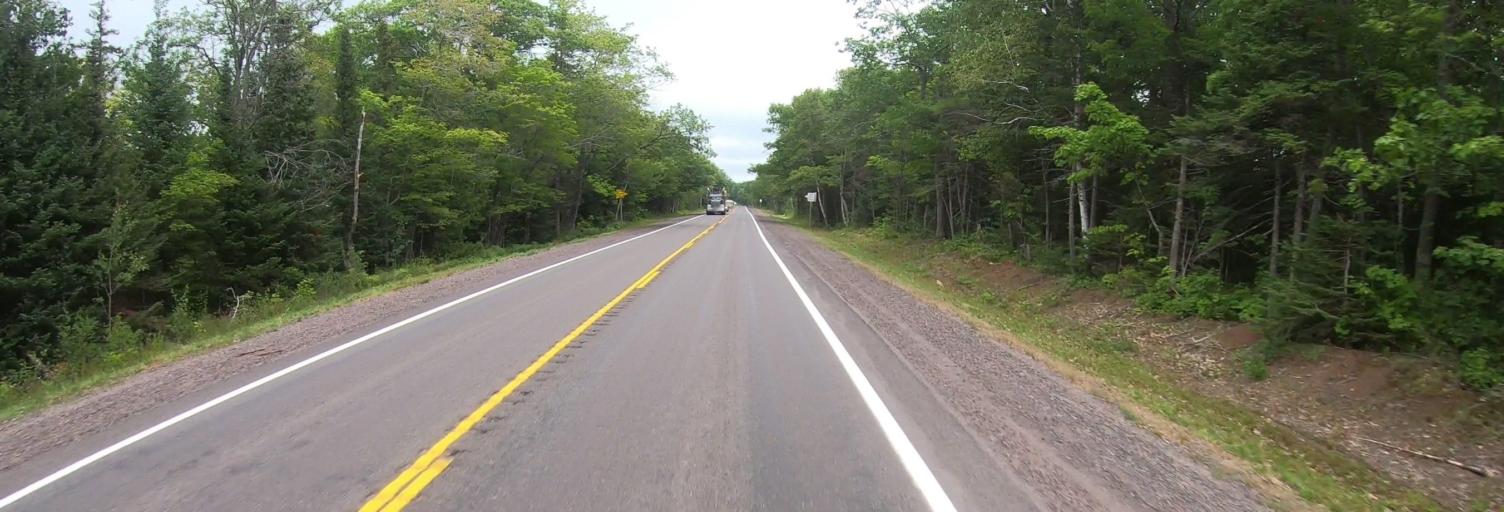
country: US
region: Michigan
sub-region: Keweenaw County
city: Eagle River
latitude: 47.3203
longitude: -88.3403
